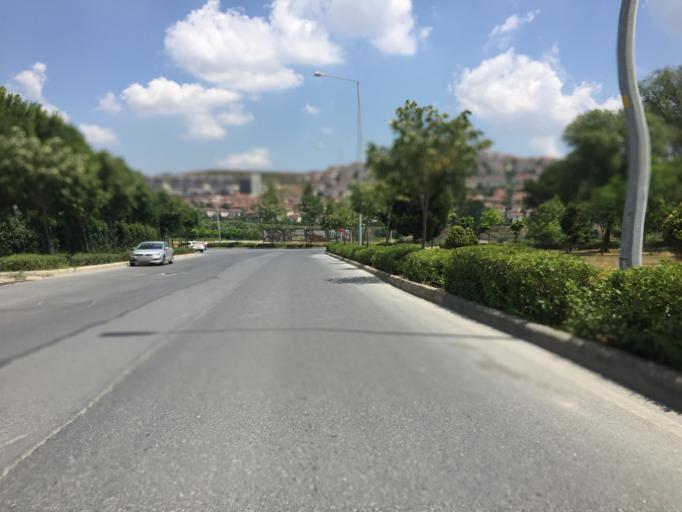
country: TR
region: Istanbul
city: Esenyurt
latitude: 41.0855
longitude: 28.6712
